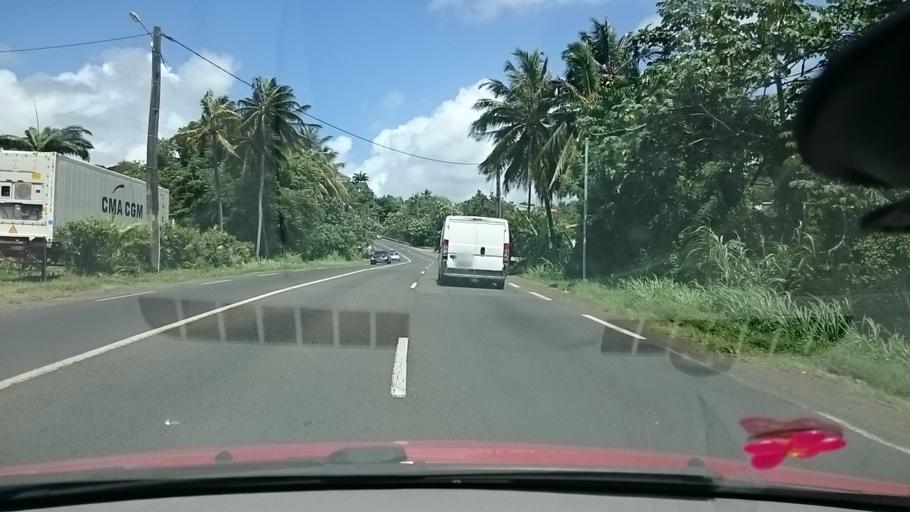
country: MQ
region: Martinique
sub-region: Martinique
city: Le Robert
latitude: 14.6710
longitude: -60.9528
